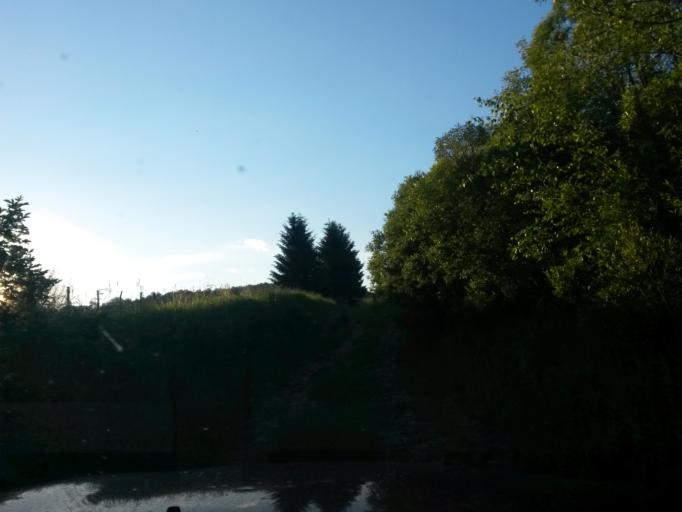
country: UA
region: Zakarpattia
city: Velykyi Bereznyi
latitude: 48.8568
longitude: 22.3564
